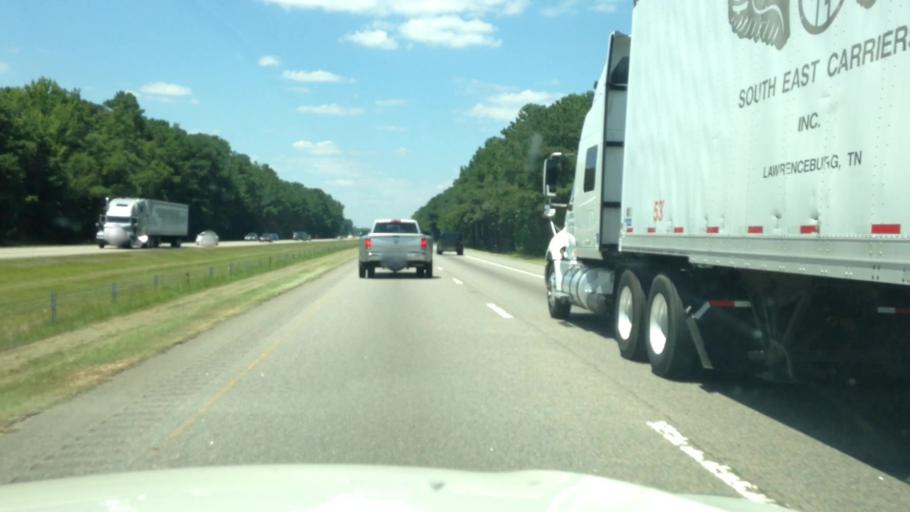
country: US
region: North Carolina
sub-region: Robeson County
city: Saint Pauls
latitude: 34.7760
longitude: -78.9957
